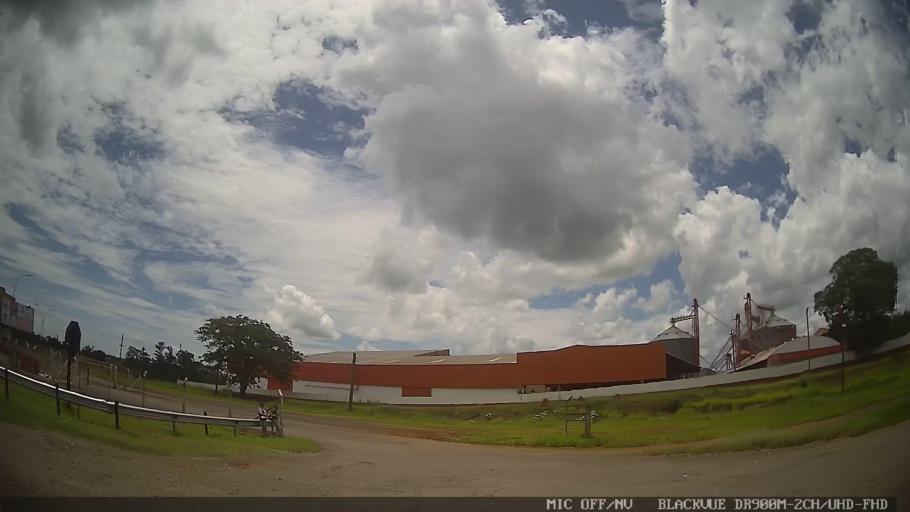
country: BR
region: Sao Paulo
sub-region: Laranjal Paulista
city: Laranjal Paulista
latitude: -23.0414
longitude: -47.9053
